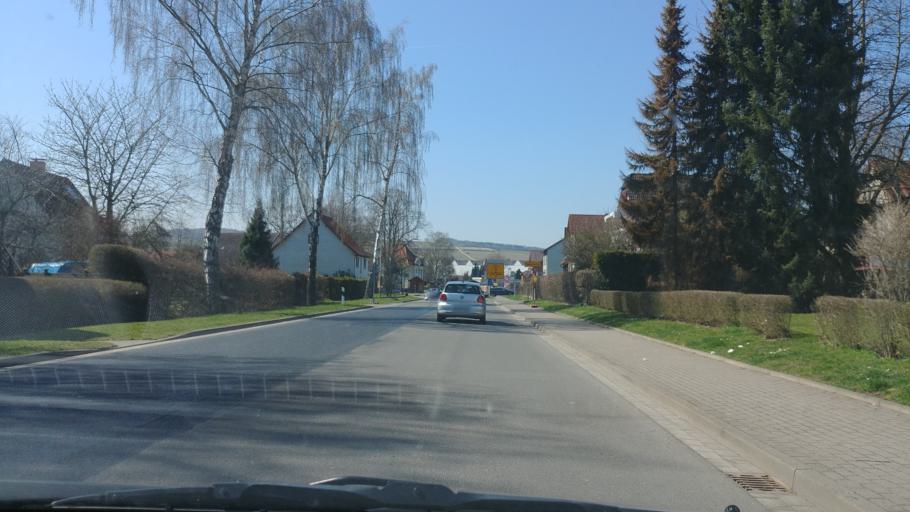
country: DE
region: Lower Saxony
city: Moringen
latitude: 51.7030
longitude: 9.8748
